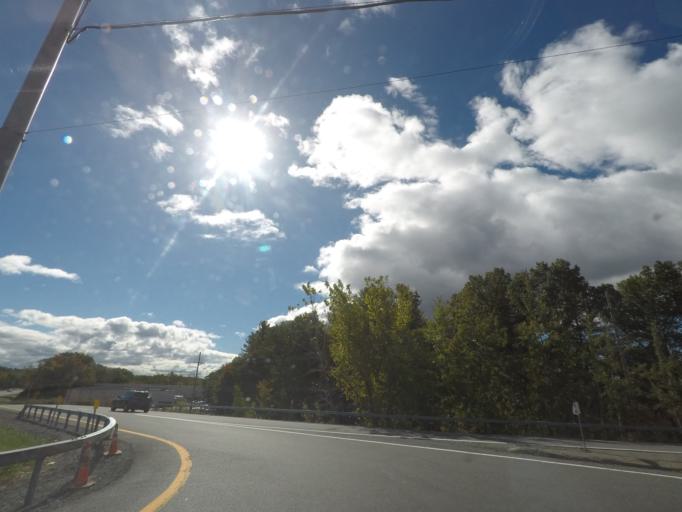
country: US
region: New York
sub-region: Saratoga County
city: Country Knolls
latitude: 42.9023
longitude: -73.7875
